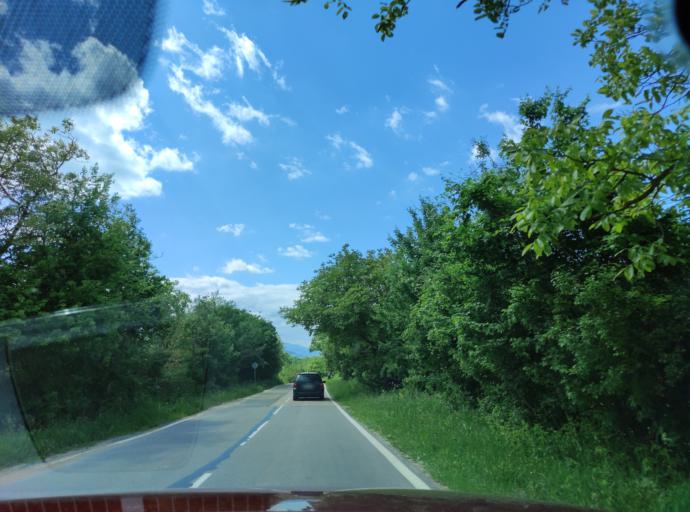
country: BG
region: Montana
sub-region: Obshtina Chiprovtsi
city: Chiprovtsi
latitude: 43.4838
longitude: 22.8224
